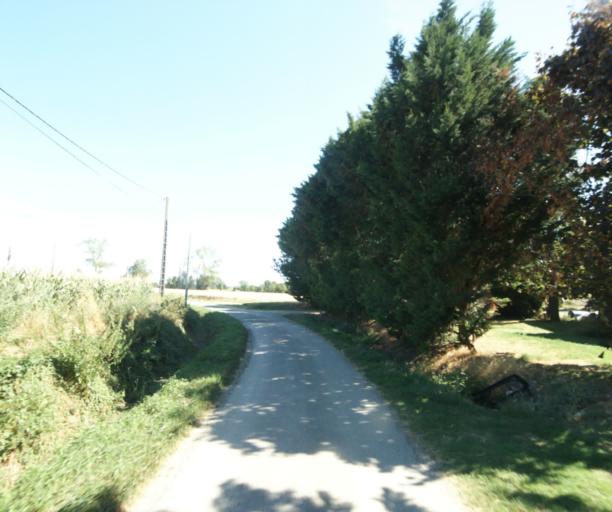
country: FR
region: Midi-Pyrenees
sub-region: Departement de la Haute-Garonne
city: Saint-Felix-Lauragais
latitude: 43.4997
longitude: 1.8974
